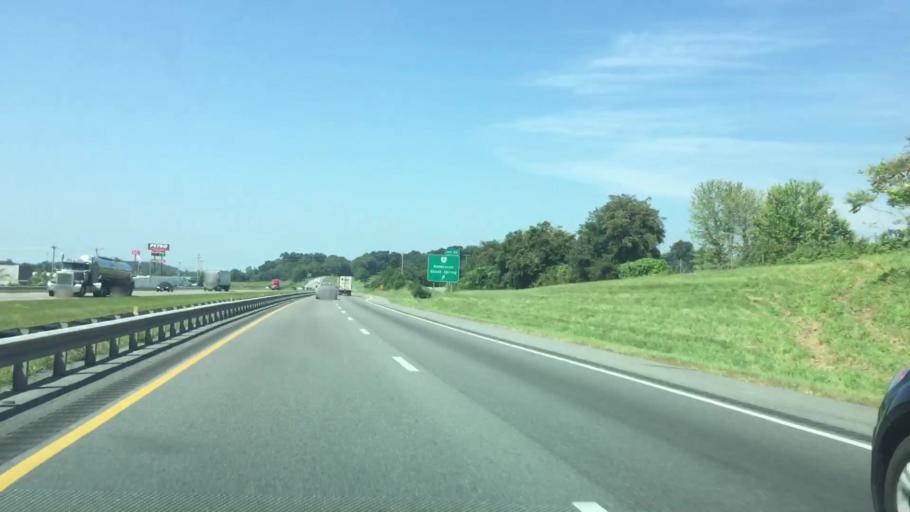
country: US
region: Virginia
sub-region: Washington County
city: Glade Spring
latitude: 36.7739
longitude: -81.7747
